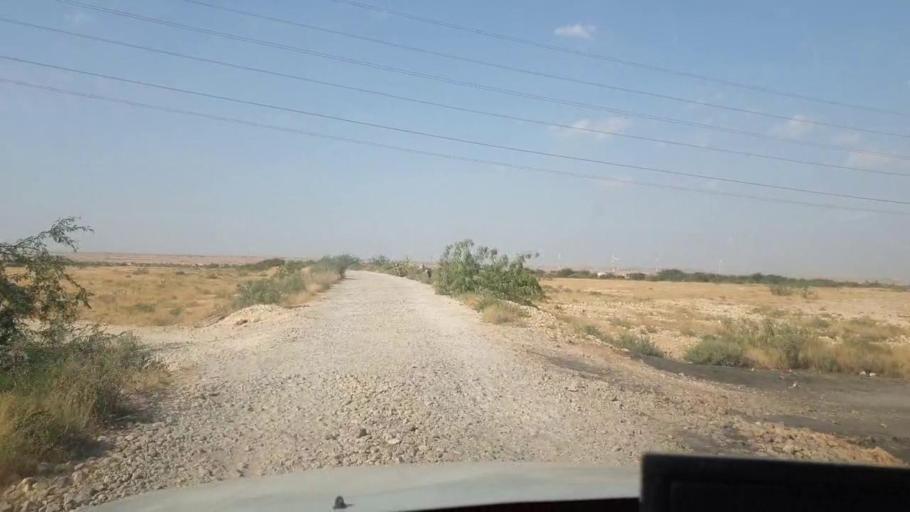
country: PK
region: Sindh
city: Daro Mehar
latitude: 25.0704
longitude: 68.0974
